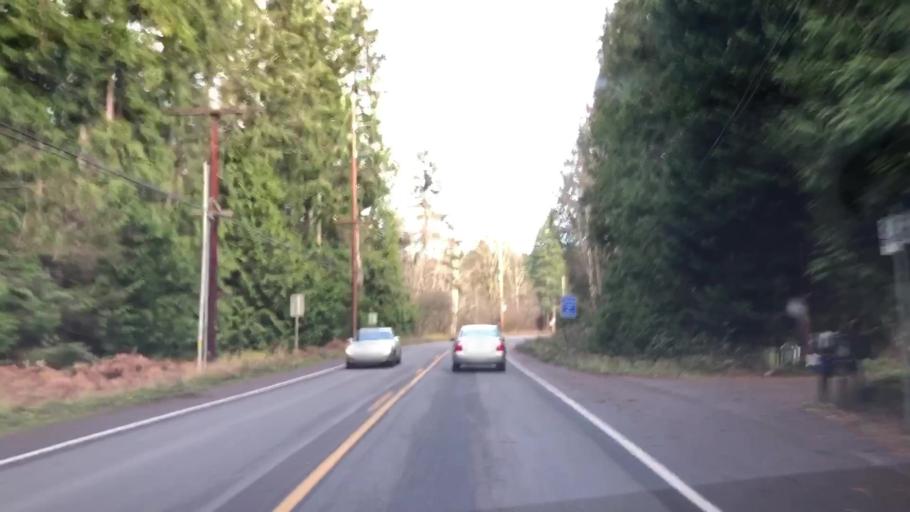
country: US
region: Washington
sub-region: Kitsap County
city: Suquamish
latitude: 47.7207
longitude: -122.5699
